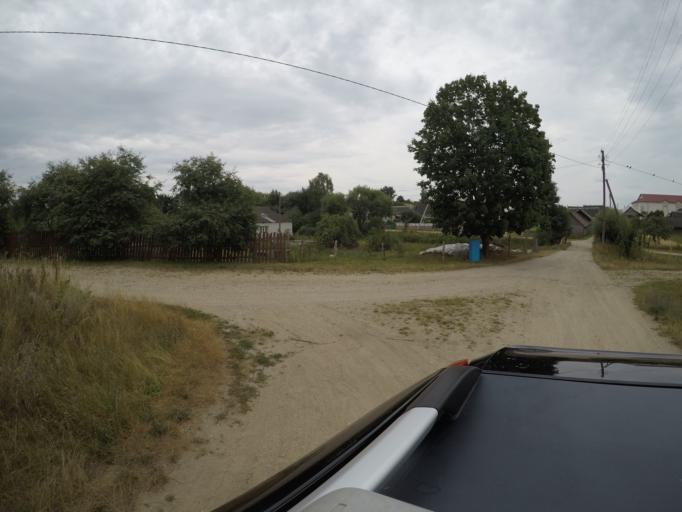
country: BY
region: Grodnenskaya
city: Hal'shany
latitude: 54.2593
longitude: 26.0105
